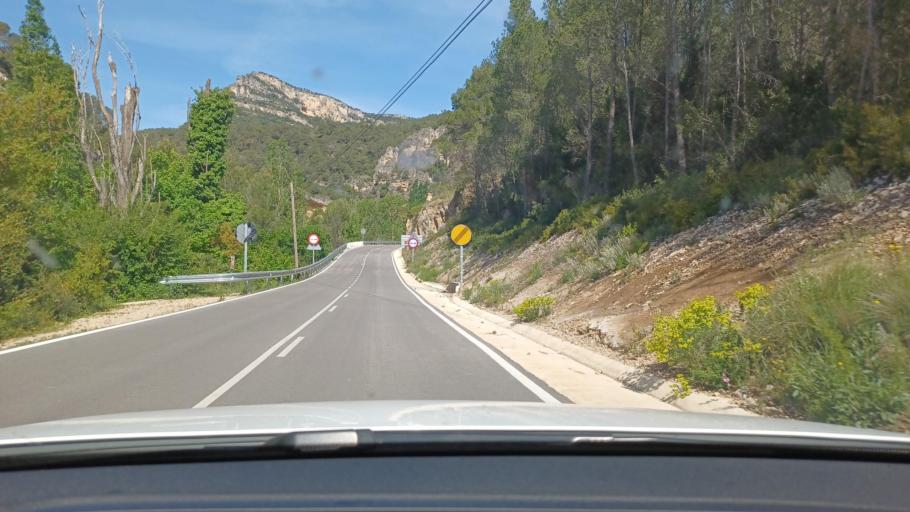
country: ES
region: Valencia
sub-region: Provincia de Castello
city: Rosell
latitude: 40.6709
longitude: 0.2409
